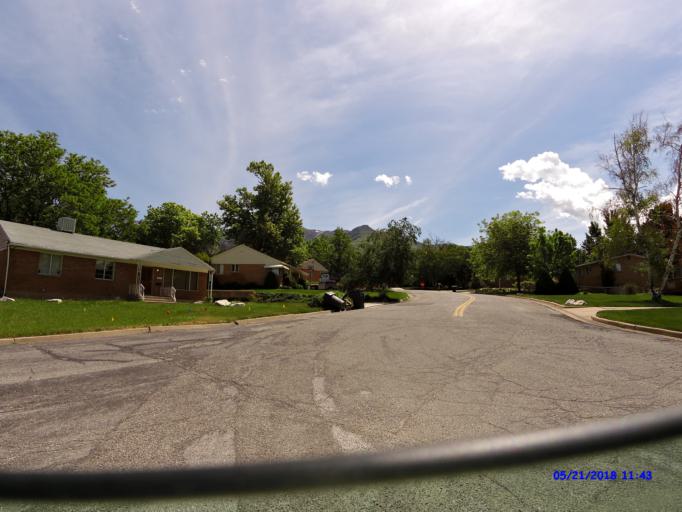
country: US
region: Utah
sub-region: Weber County
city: South Ogden
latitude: 41.1949
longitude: -111.9555
